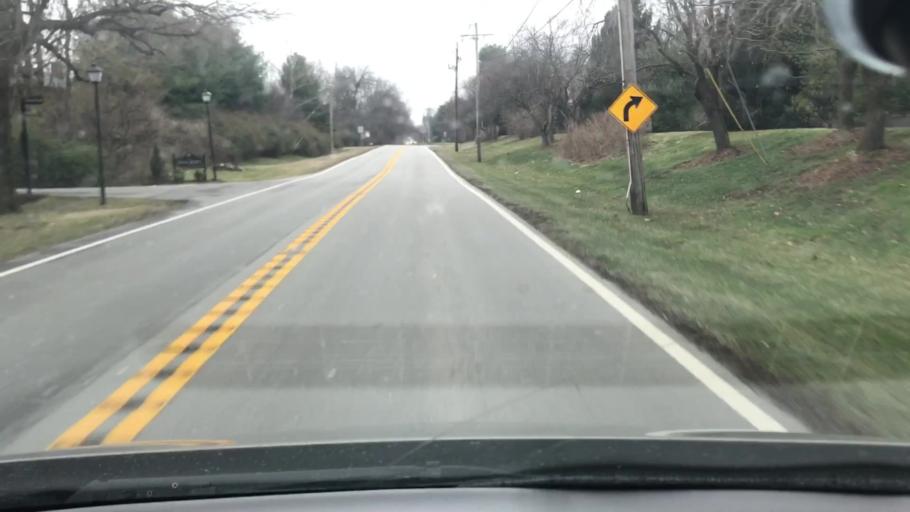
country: US
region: Kentucky
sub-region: Jefferson County
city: Barbourmeade
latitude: 38.2897
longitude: -85.6176
